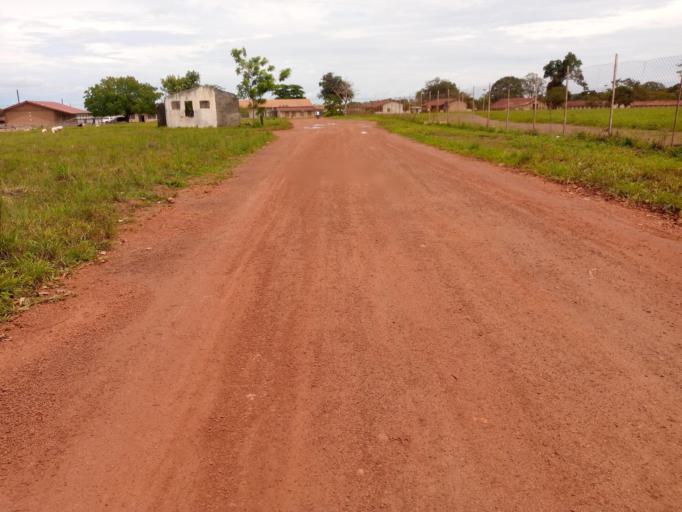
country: SL
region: Southern Province
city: Largo
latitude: 8.1161
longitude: -12.0691
